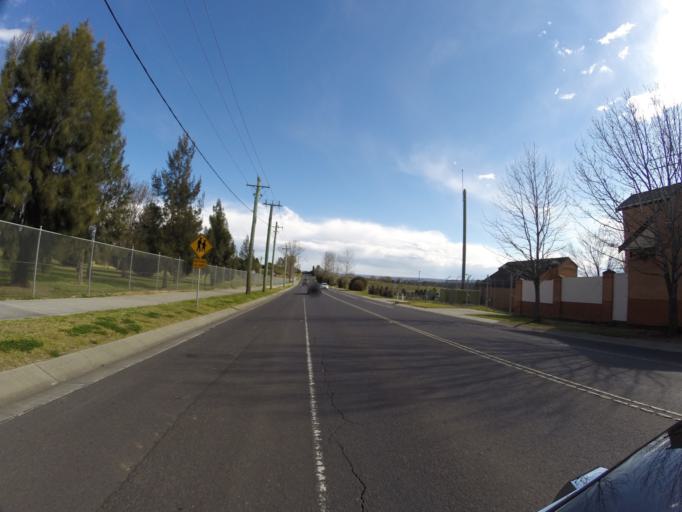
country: AU
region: New South Wales
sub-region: Camden
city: Narellan
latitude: -34.0441
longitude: 150.7245
